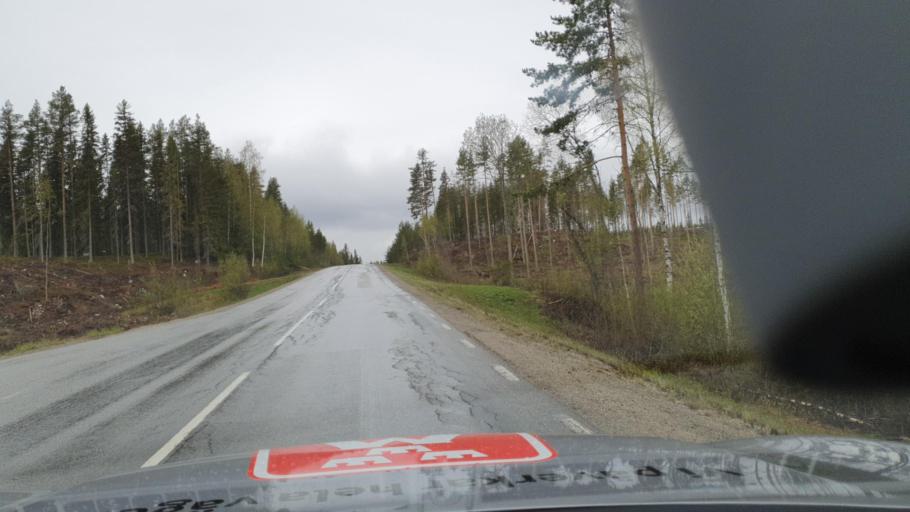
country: SE
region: Vaesternorrland
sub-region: OErnskoeldsviks Kommun
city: Bredbyn
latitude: 63.4825
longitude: 17.8899
